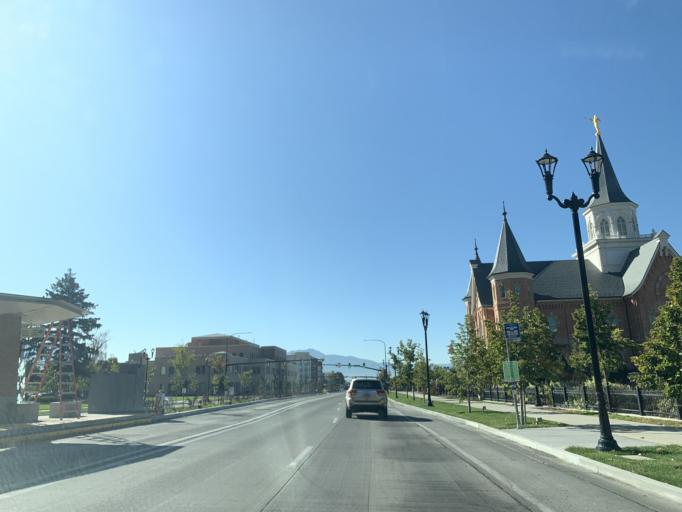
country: US
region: Utah
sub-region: Utah County
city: Provo
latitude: 40.2334
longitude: -111.6588
